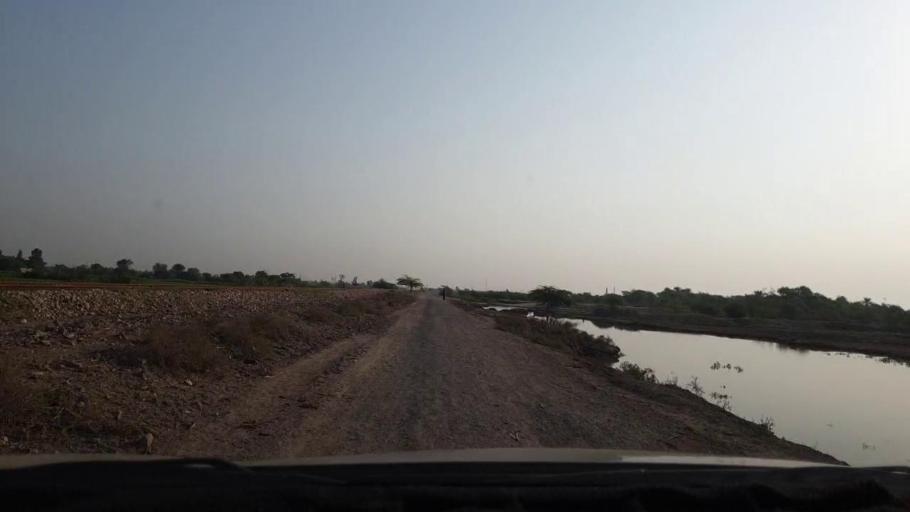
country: PK
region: Sindh
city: Larkana
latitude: 27.5199
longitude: 68.1908
